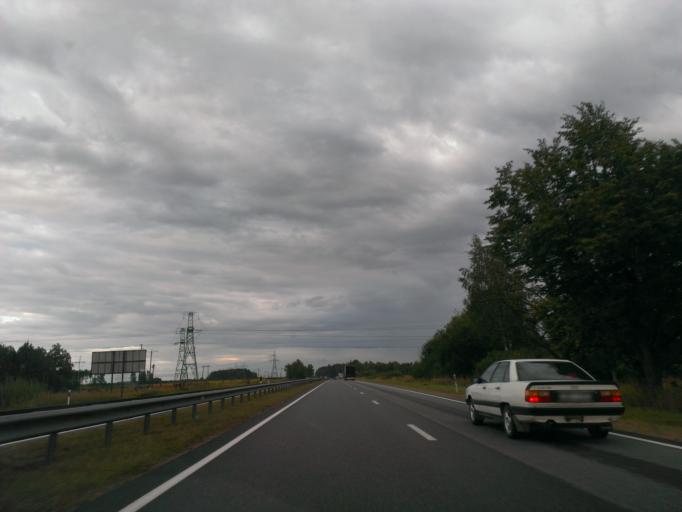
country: LV
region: Salaspils
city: Salaspils
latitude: 56.8462
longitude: 24.3719
